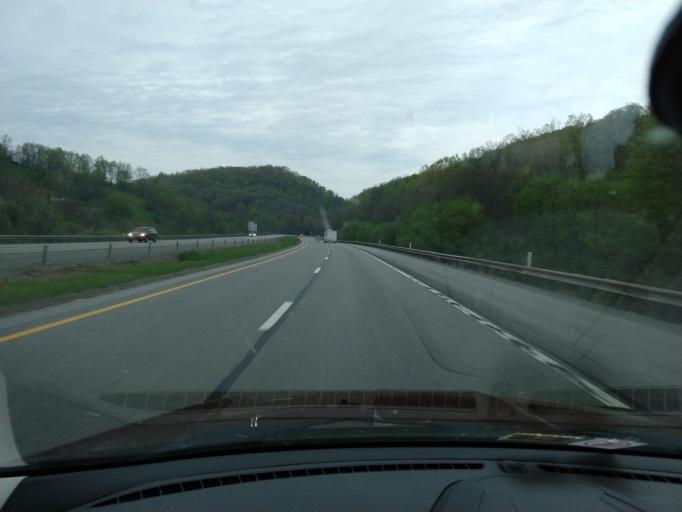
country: US
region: West Virginia
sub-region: Lewis County
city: Weston
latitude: 38.9734
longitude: -80.5110
